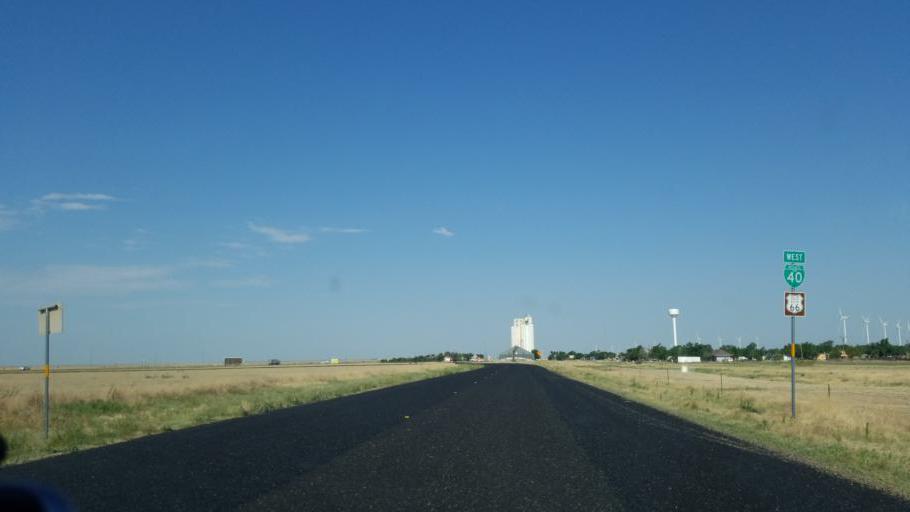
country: US
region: Texas
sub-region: Oldham County
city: Vega
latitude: 35.2719
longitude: -102.6575
